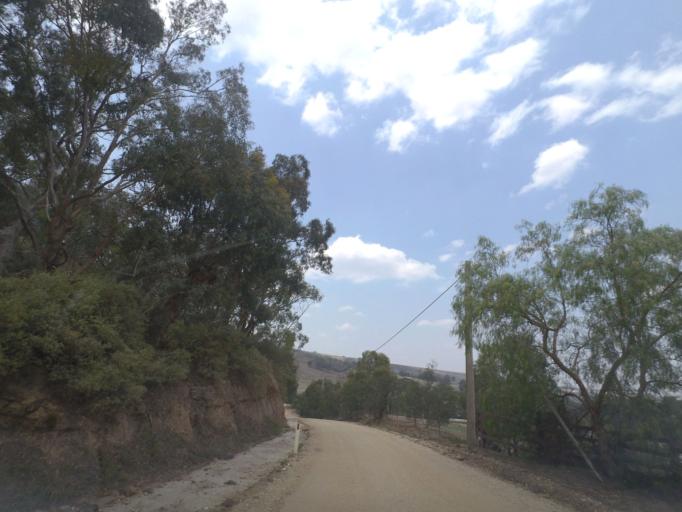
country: AU
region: Victoria
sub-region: Moorabool
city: Bacchus Marsh
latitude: -37.6046
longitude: 144.4500
